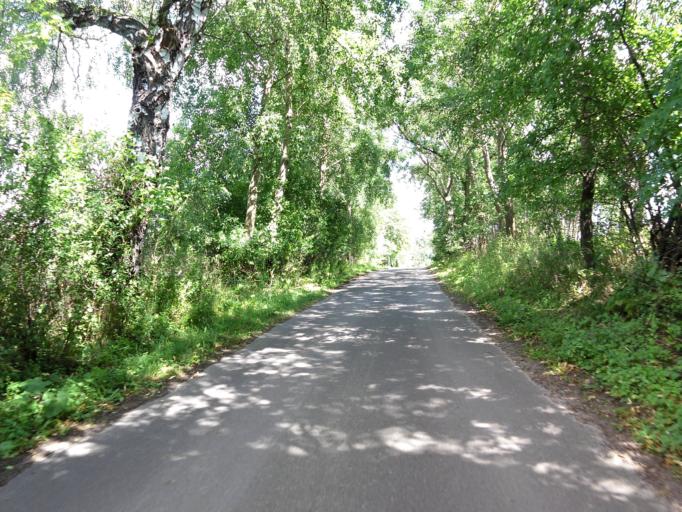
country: DE
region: Brandenburg
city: Lychen
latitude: 53.2787
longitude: 13.4462
